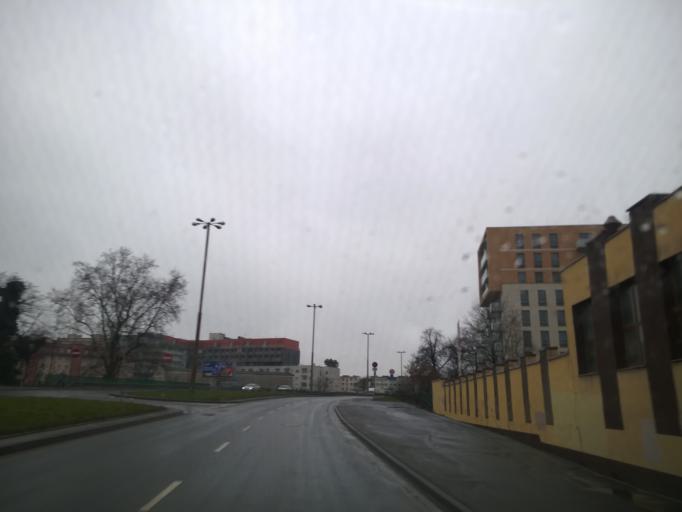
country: PL
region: Lower Silesian Voivodeship
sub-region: Powiat wroclawski
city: Wroclaw
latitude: 51.1171
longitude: 17.0207
